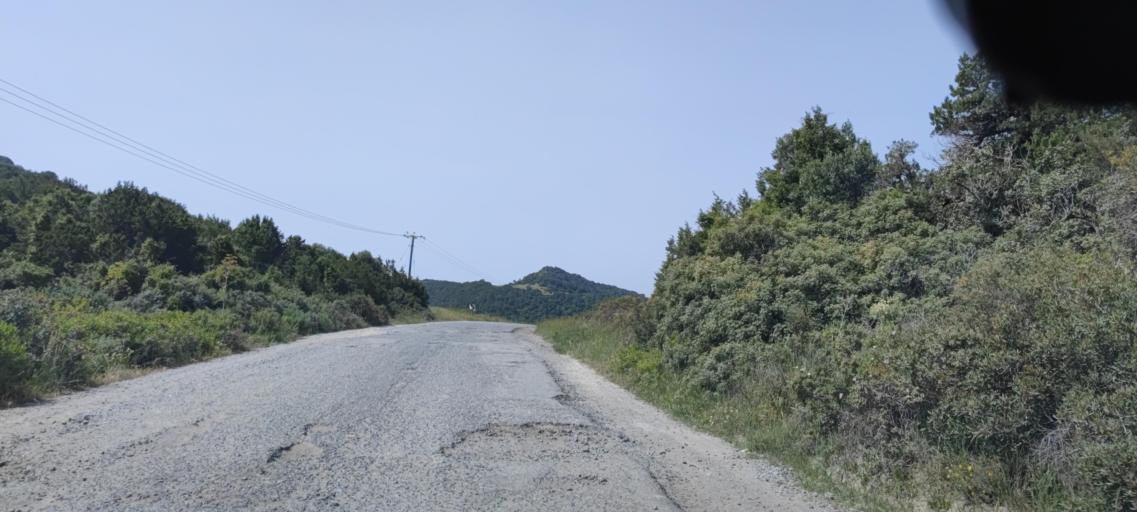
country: CY
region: Ammochostos
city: Rizokarpaso
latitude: 35.6138
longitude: 34.4528
